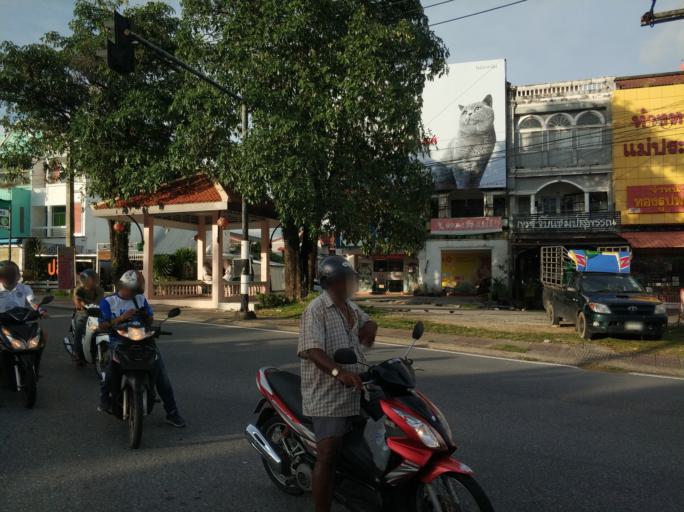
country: TH
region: Phuket
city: Kathu
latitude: 7.8993
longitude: 98.3512
